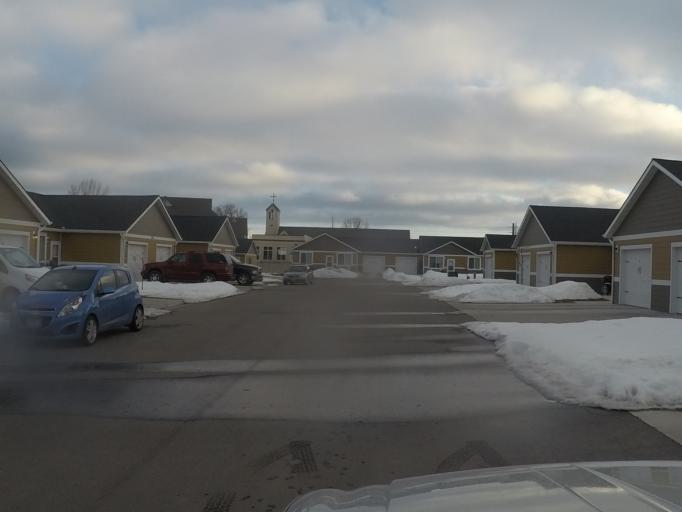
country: US
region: Montana
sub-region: Yellowstone County
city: Billings
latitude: 45.7866
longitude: -108.6220
